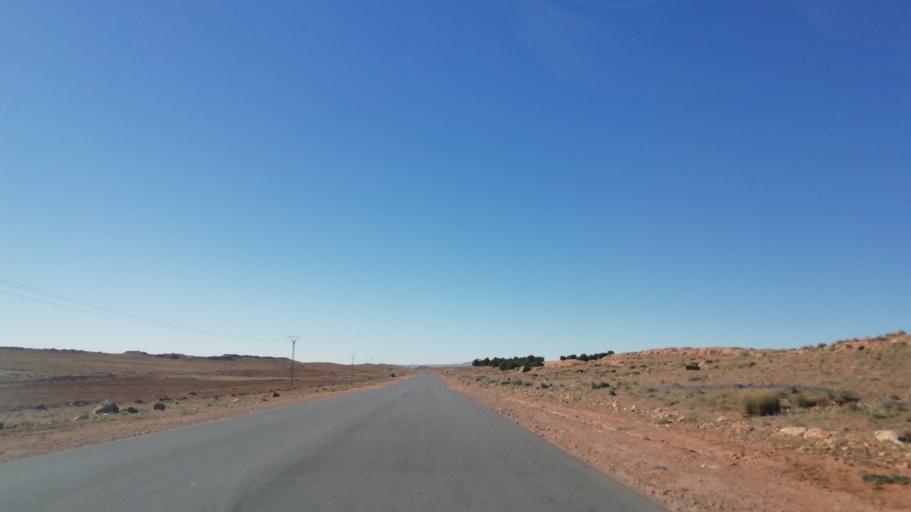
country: DZ
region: El Bayadh
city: El Bayadh
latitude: 33.6489
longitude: 1.4032
